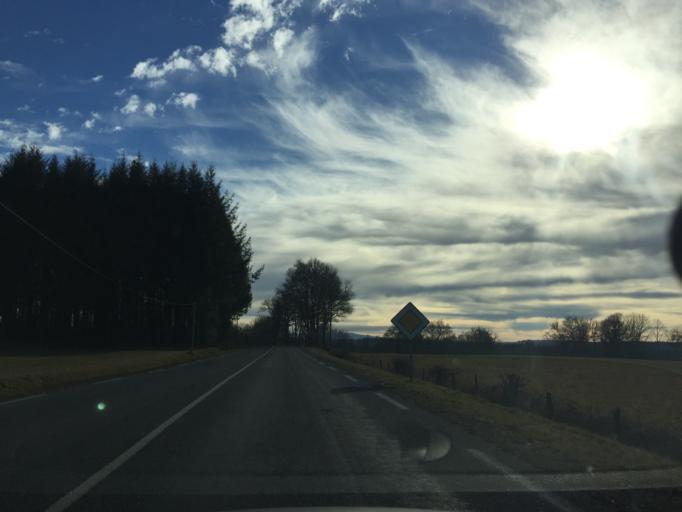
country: FR
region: Limousin
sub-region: Departement de la Creuse
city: Auzances
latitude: 45.8795
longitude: 2.5037
